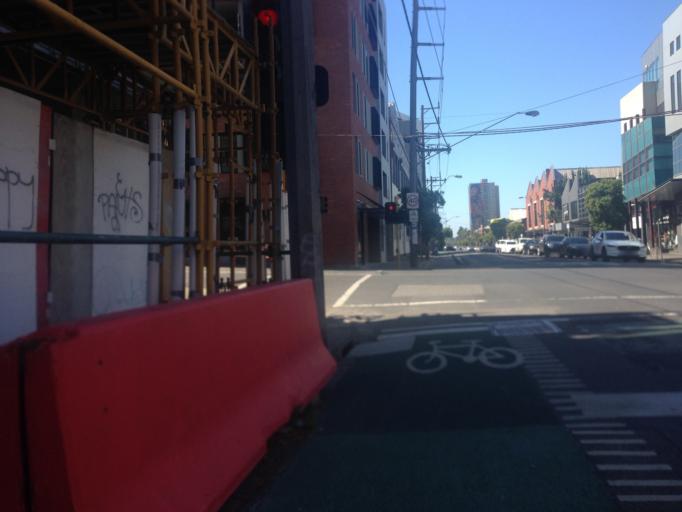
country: AU
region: Victoria
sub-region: Yarra
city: Collingwood
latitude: -37.8070
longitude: 144.9860
